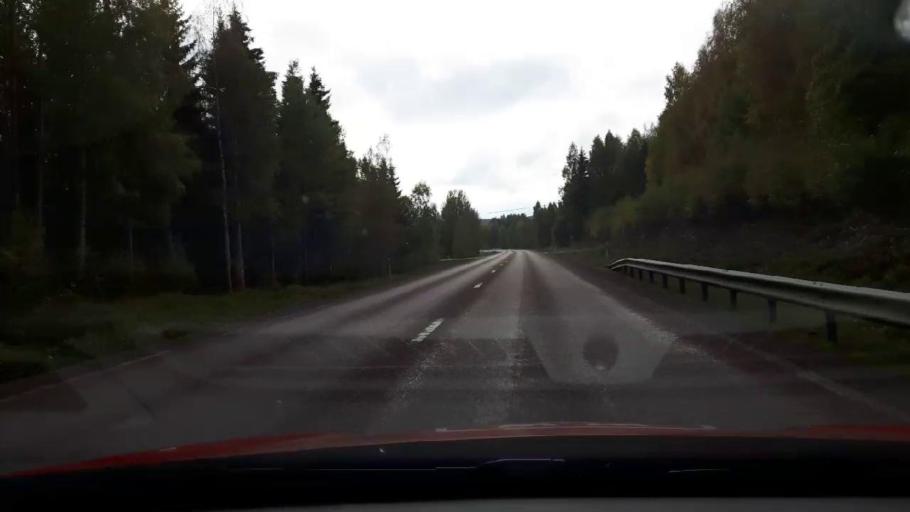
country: SE
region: Gaevleborg
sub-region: Ljusdals Kommun
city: Jaervsoe
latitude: 61.6121
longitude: 16.2953
